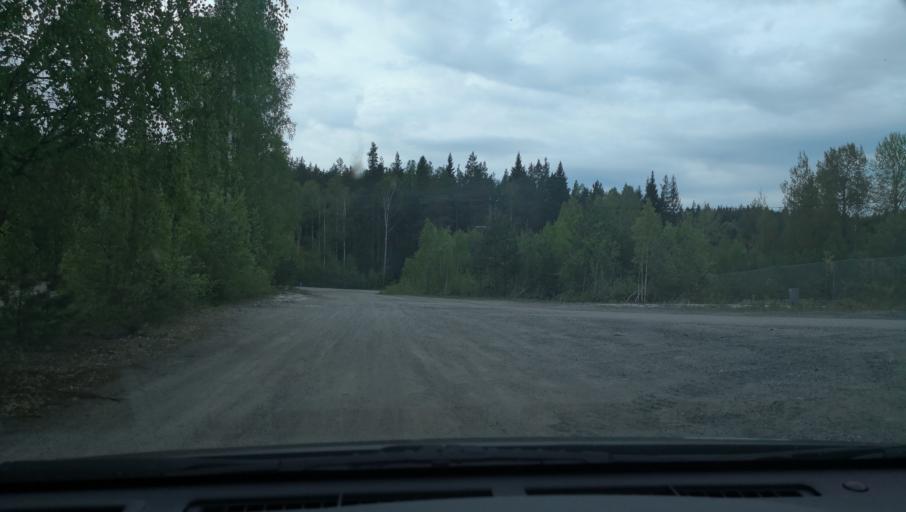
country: SE
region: Vaestmanland
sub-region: Skinnskattebergs Kommun
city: Skinnskatteberg
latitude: 59.8286
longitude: 15.5609
